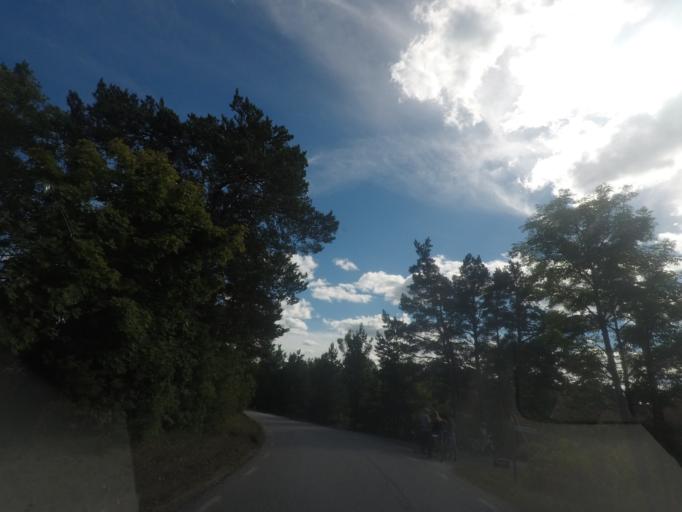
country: SE
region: Stockholm
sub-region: Norrtalje Kommun
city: Arno
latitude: 60.1637
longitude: 18.7383
